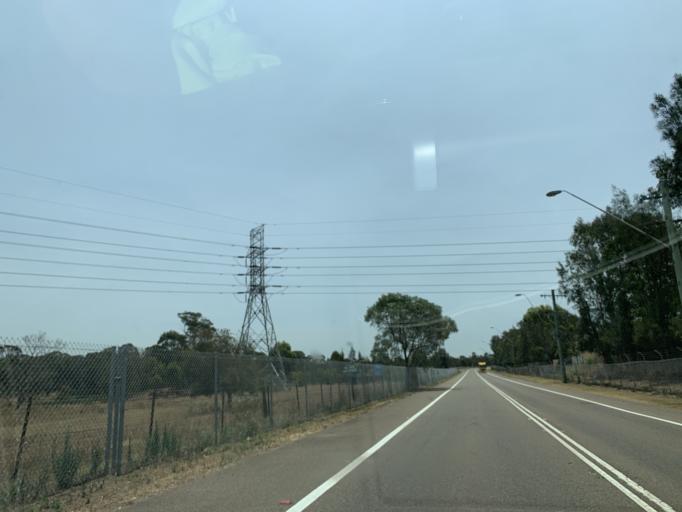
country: AU
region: New South Wales
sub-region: Blacktown
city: Doonside
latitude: -33.8061
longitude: 150.8641
